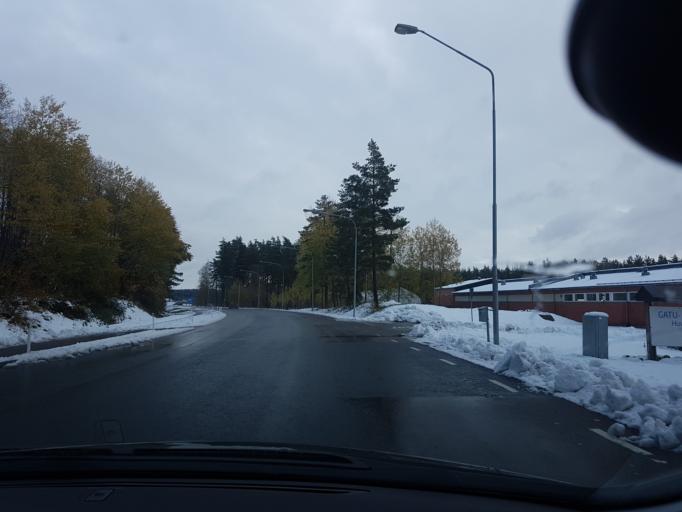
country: SE
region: Joenkoeping
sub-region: Vetlanda Kommun
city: Vetlanda
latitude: 57.4206
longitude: 15.1028
